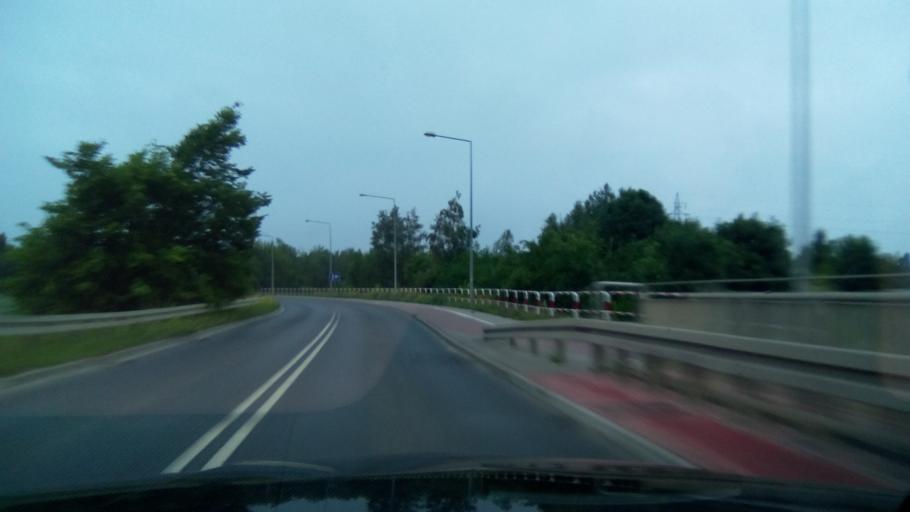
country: PL
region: Greater Poland Voivodeship
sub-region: Powiat poznanski
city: Swarzedz
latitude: 52.4255
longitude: 17.0804
